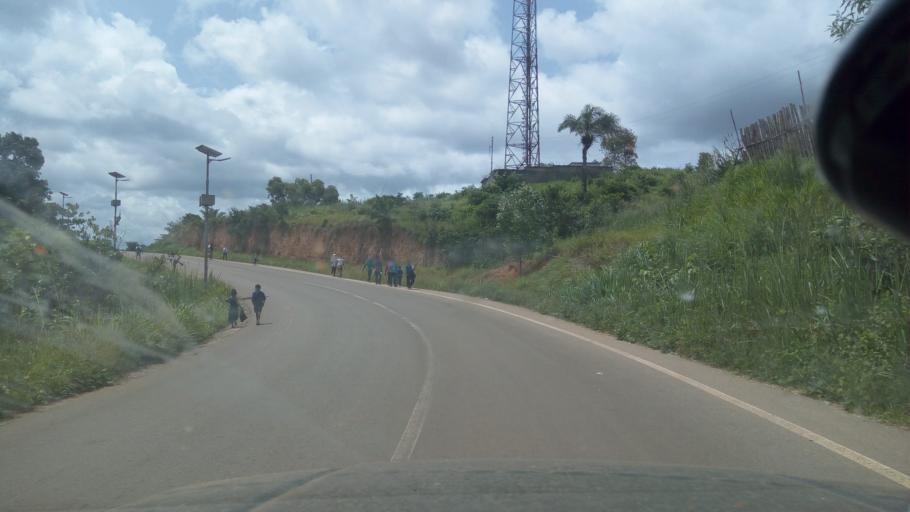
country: SL
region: Eastern Province
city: Kenema
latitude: 7.8761
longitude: -11.1747
